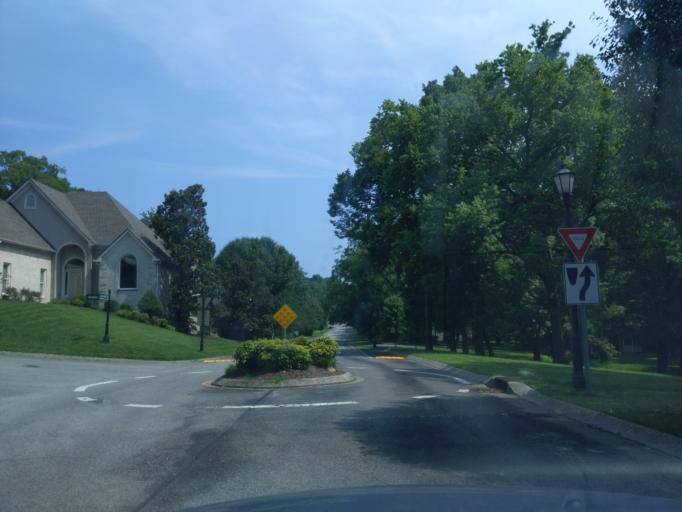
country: US
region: Tennessee
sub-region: Williamson County
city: Brentwood Estates
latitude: 36.0388
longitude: -86.7488
